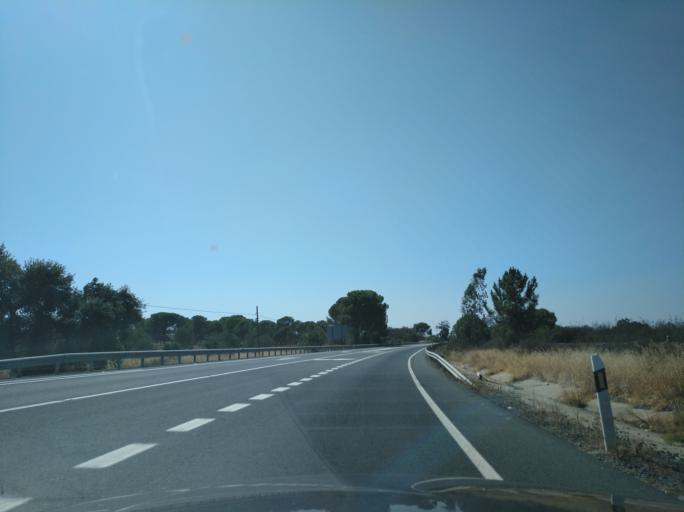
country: ES
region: Andalusia
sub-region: Provincia de Huelva
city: San Bartolome de la Torre
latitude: 37.4292
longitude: -7.0551
